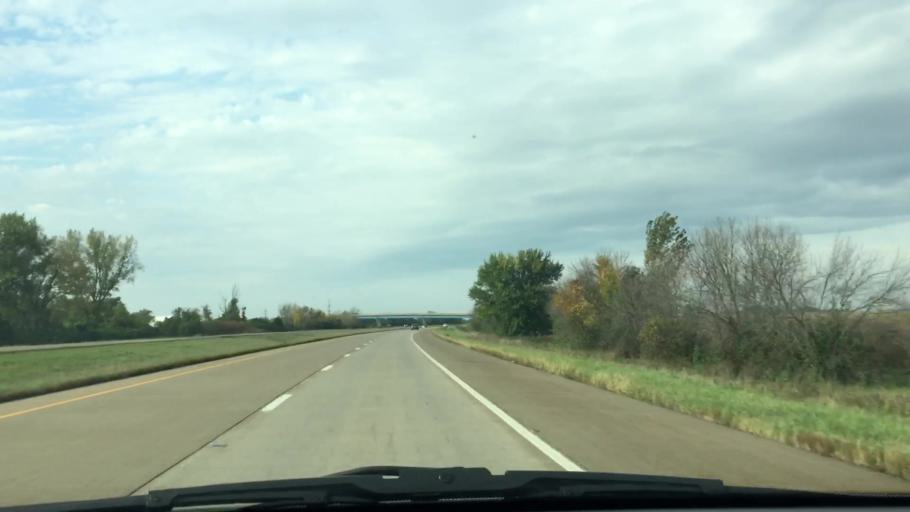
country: US
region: Illinois
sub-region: Whiteside County
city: Prophetstown
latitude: 41.7551
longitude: -89.8572
